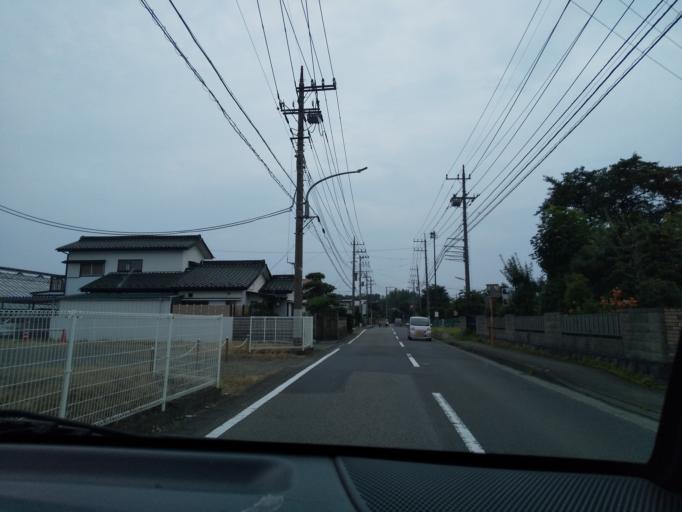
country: JP
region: Kanagawa
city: Atsugi
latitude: 35.4142
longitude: 139.3912
